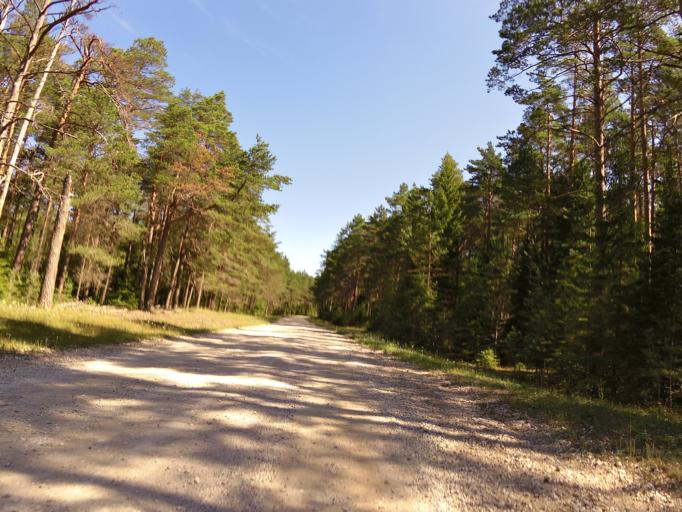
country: EE
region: Hiiumaa
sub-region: Kaerdla linn
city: Kardla
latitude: 58.9172
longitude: 22.3442
